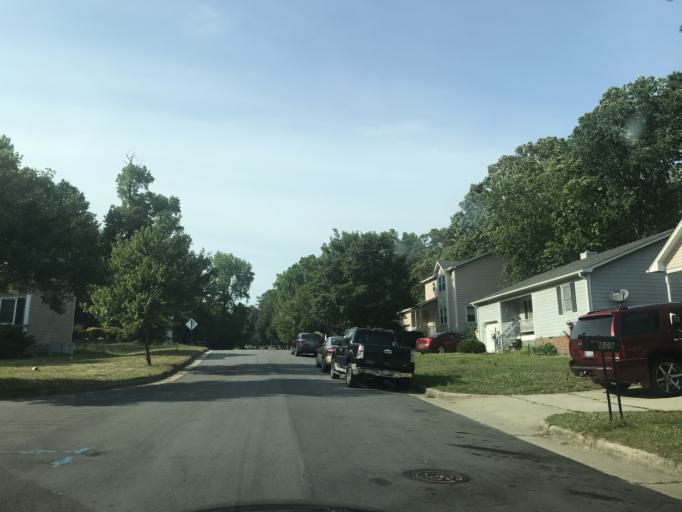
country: US
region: North Carolina
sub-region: Wake County
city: Raleigh
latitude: 35.7686
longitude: -78.5872
